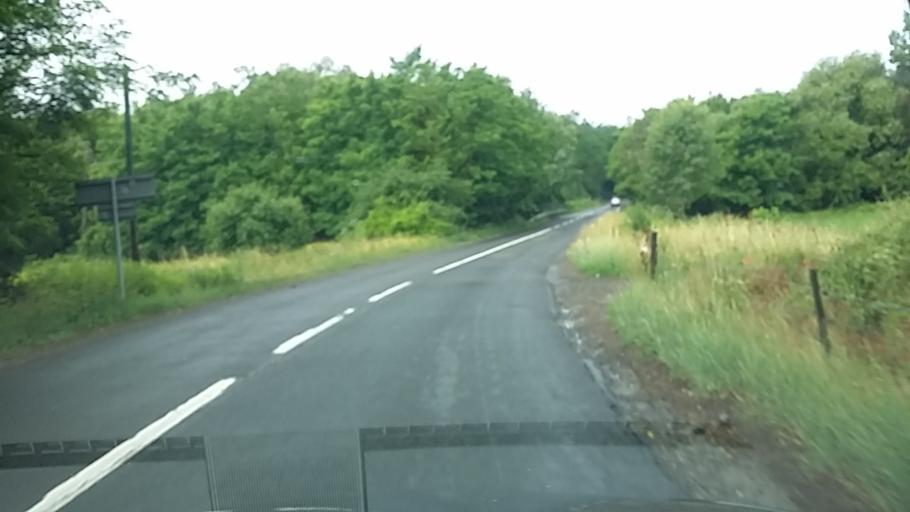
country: SK
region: Nitriansky
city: Sahy
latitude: 47.9852
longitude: 18.8110
